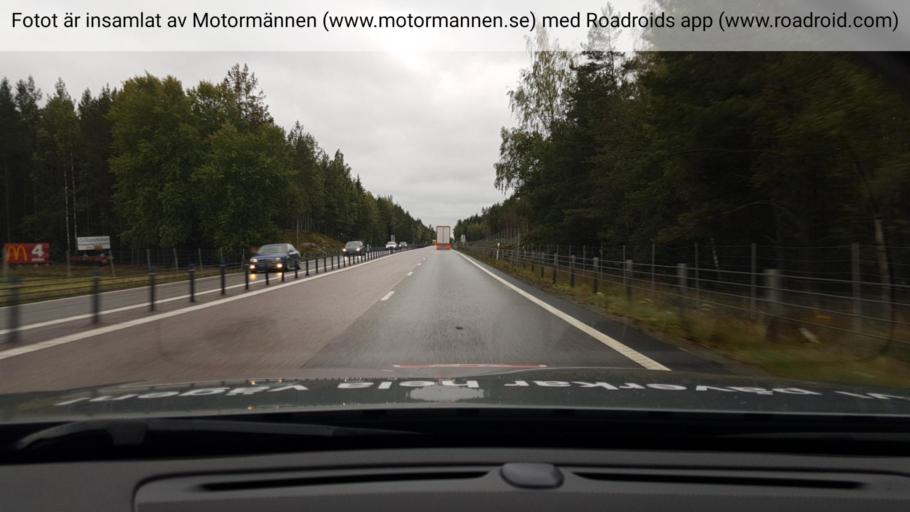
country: SE
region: Vaestmanland
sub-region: Kopings Kommun
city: Koping
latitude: 59.5466
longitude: 16.0125
